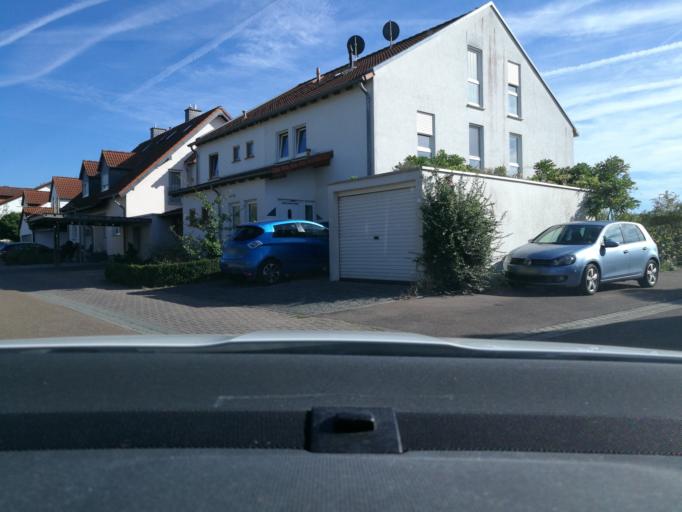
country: DE
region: Rheinland-Pfalz
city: Netzbach
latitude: 50.3662
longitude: 8.1010
